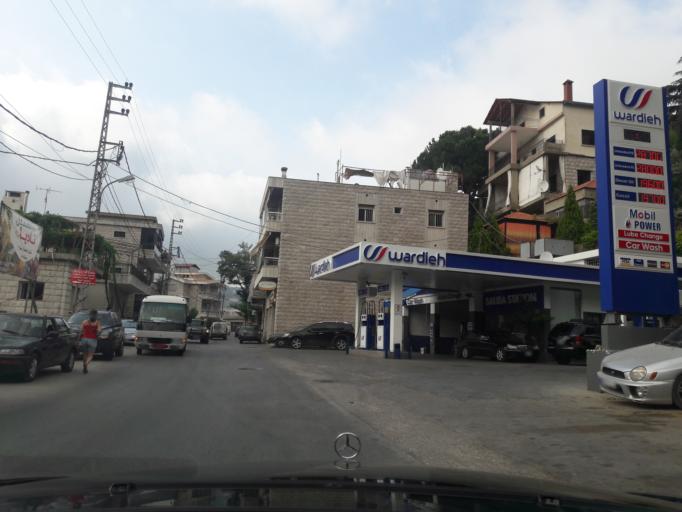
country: LB
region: Mont-Liban
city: Djounie
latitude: 33.9282
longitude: 35.7417
